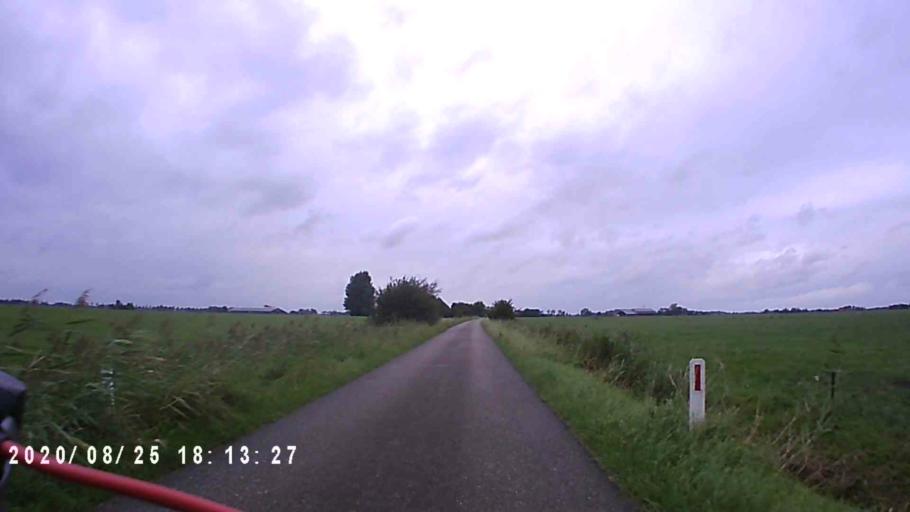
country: NL
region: Groningen
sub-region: Gemeente Zuidhorn
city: Oldehove
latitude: 53.2935
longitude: 6.4357
